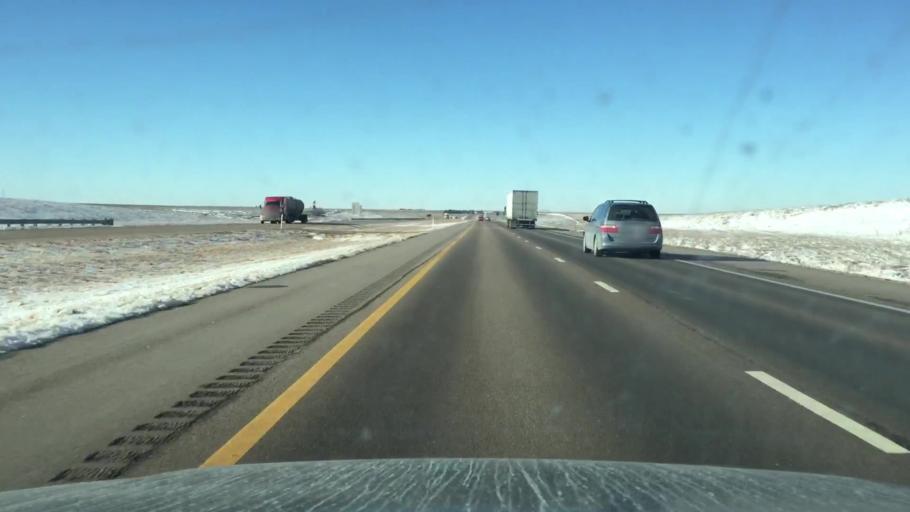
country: US
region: Kansas
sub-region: Logan County
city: Oakley
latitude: 39.1338
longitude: -100.8209
